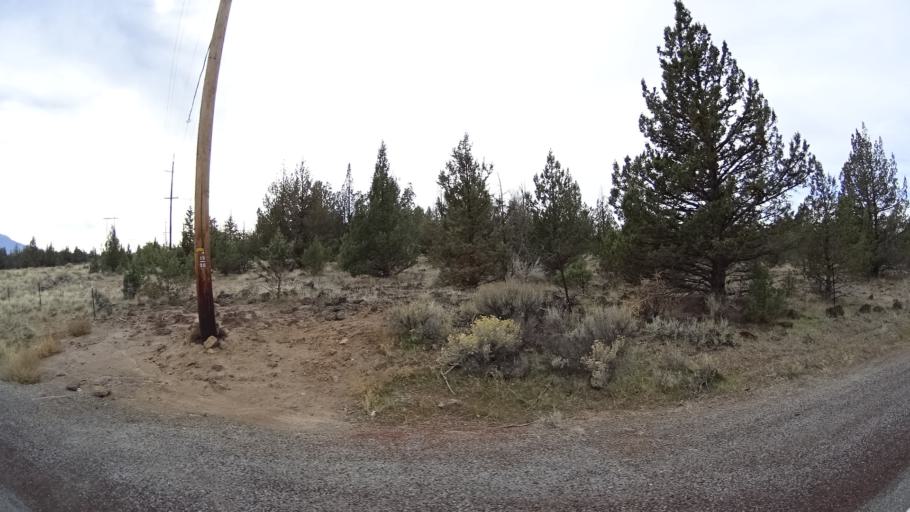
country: US
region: California
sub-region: Siskiyou County
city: Weed
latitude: 41.6083
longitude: -122.3644
